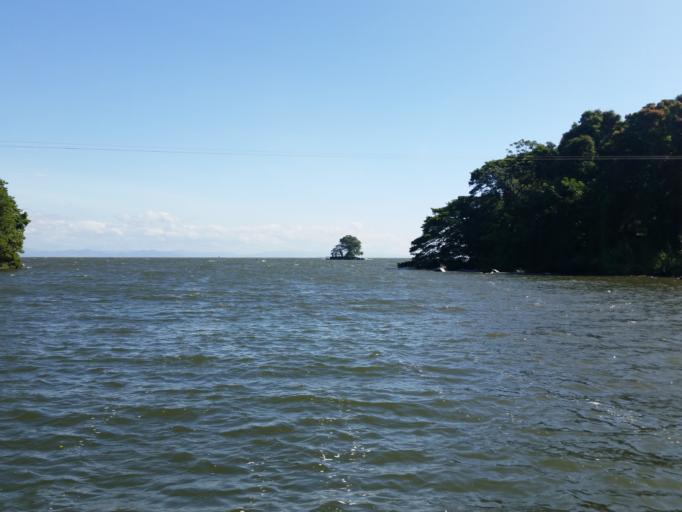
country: NI
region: Granada
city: Granada
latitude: 11.8970
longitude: -85.8949
